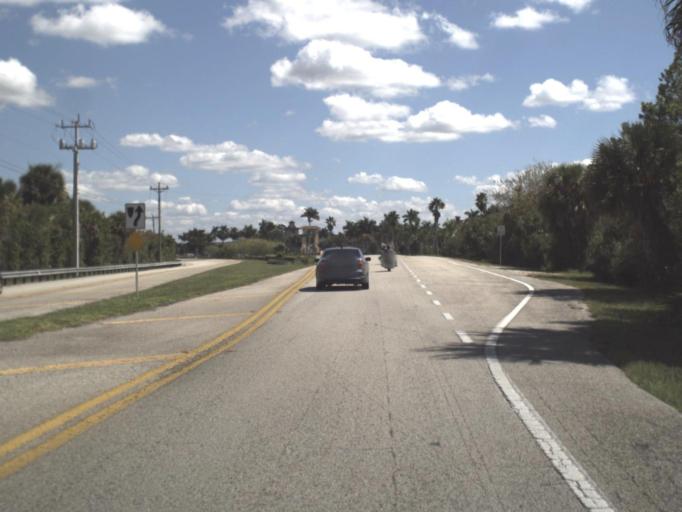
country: US
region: Florida
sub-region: Collier County
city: Marco
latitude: 25.9603
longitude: -81.5153
